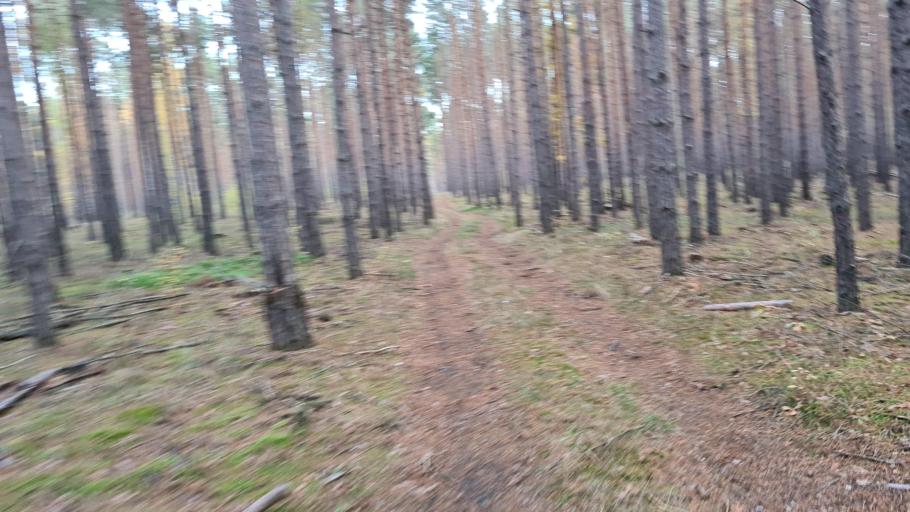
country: DE
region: Brandenburg
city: Trobitz
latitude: 51.5686
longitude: 13.4286
